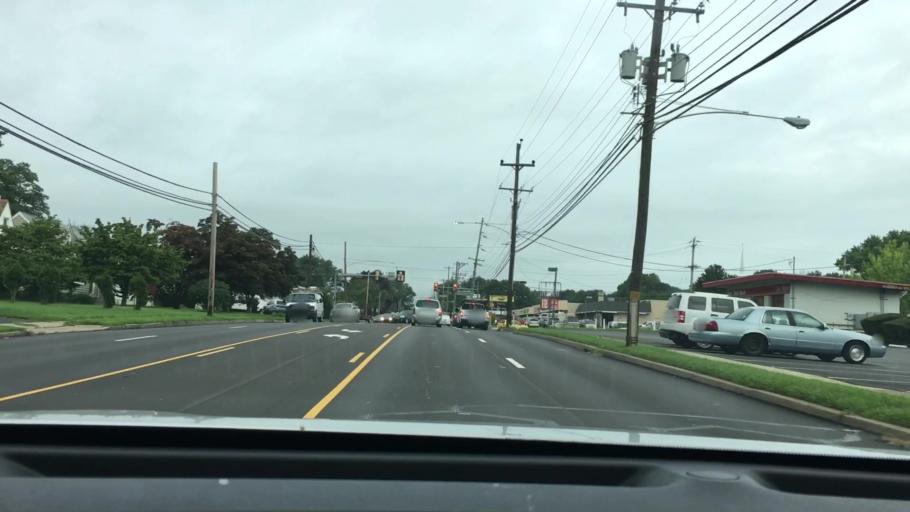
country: US
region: Pennsylvania
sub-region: Bucks County
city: Warminster Heights
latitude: 40.1791
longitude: -75.0845
